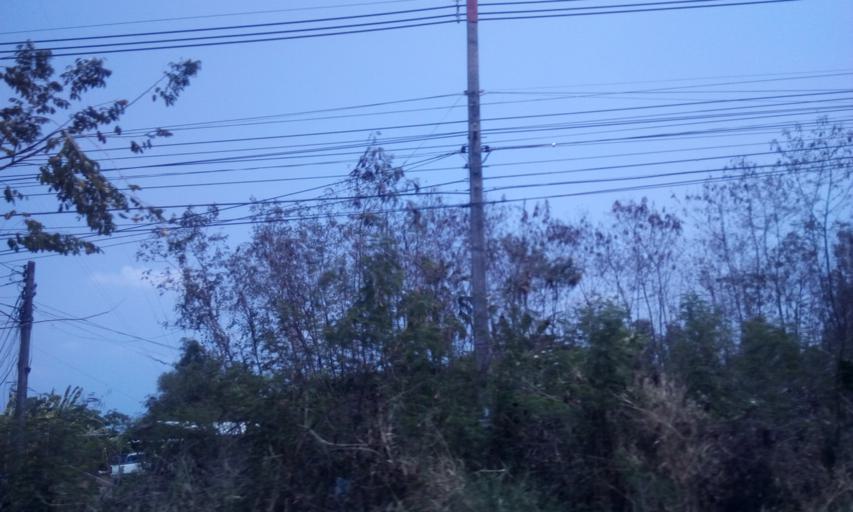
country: TH
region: Chachoengsao
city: Bang Nam Priao
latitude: 13.7744
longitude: 101.0647
